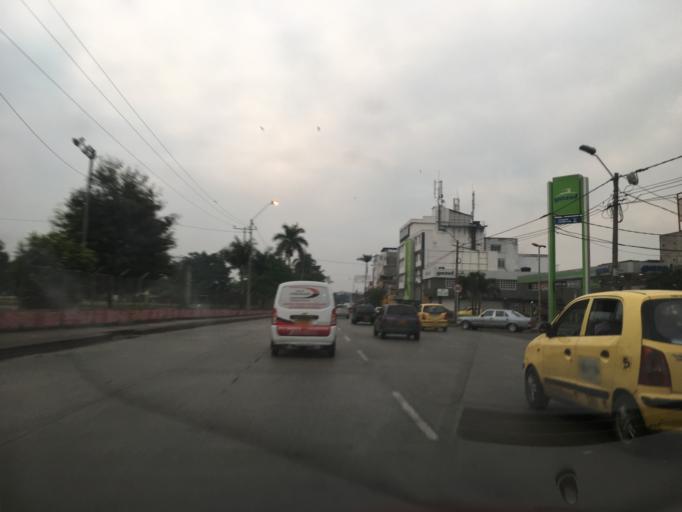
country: CO
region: Valle del Cauca
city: Cali
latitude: 3.4523
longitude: -76.5189
